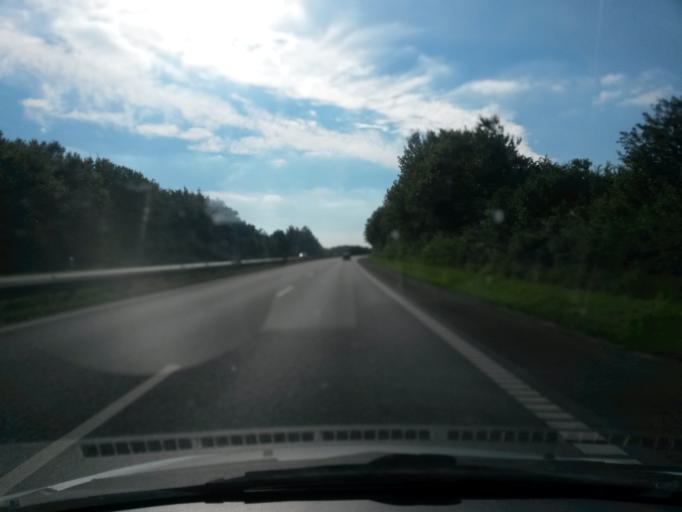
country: DK
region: Central Jutland
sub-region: Arhus Kommune
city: Logten
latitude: 56.2661
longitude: 10.3281
